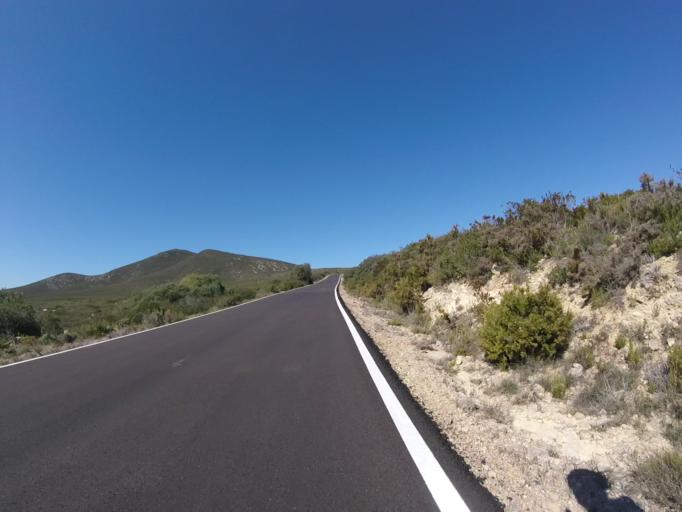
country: ES
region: Valencia
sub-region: Provincia de Castello
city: Cervera del Maestre
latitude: 40.4006
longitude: 0.2338
